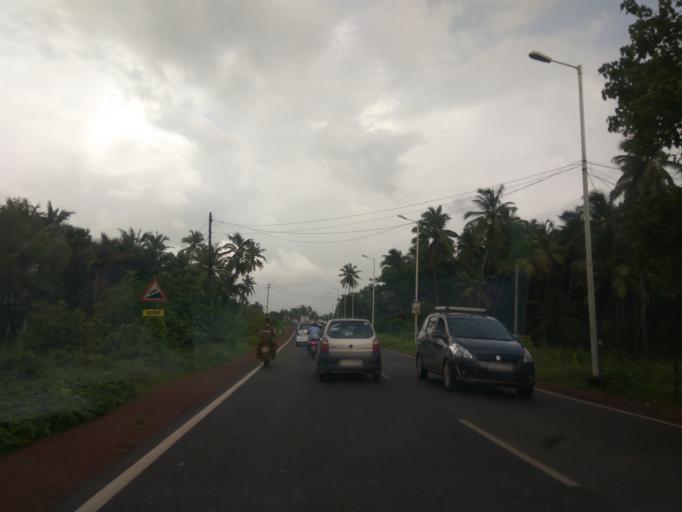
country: IN
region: Goa
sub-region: North Goa
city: Goa Velha
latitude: 15.4261
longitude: 73.8945
